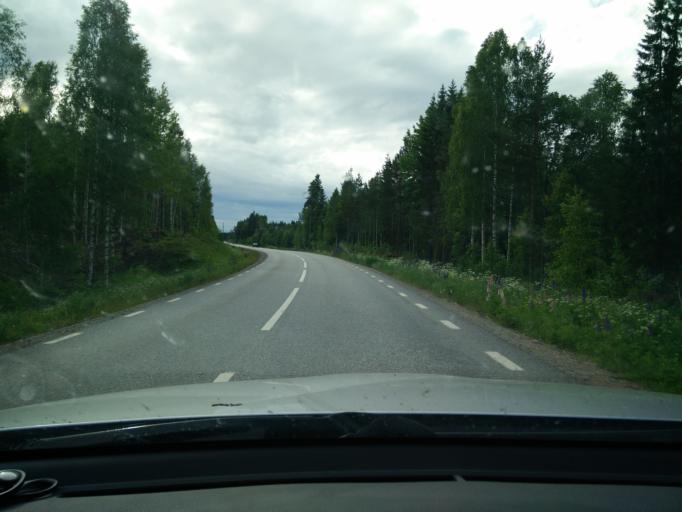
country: SE
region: Gaevleborg
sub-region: Nordanstigs Kommun
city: Bergsjoe
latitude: 62.0966
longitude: 16.7601
